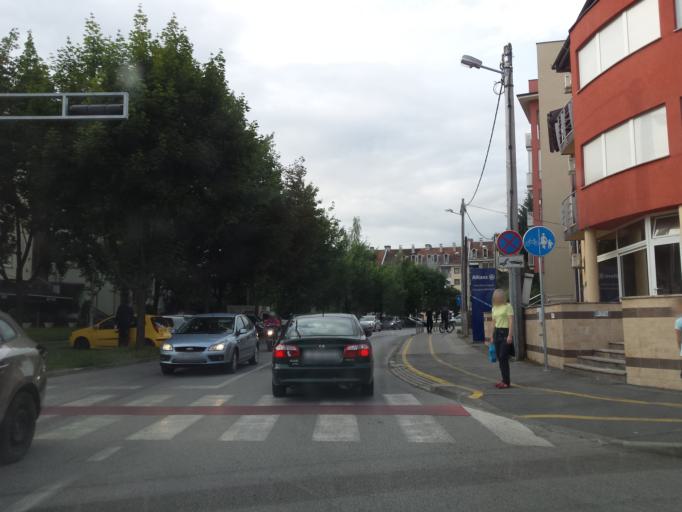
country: HR
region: Grad Zagreb
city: Jankomir
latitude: 45.8053
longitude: 15.9021
